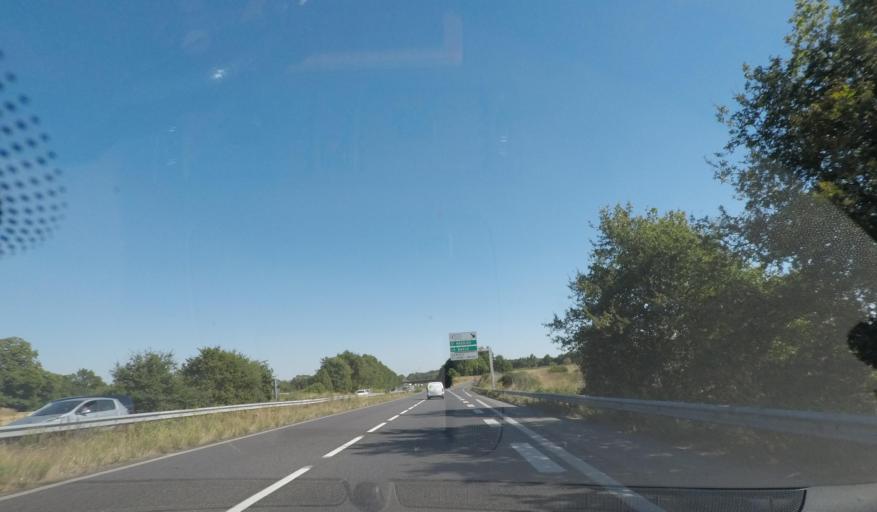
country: FR
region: Pays de la Loire
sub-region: Departement de la Loire-Atlantique
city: Pontchateau
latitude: 47.4399
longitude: -2.0771
